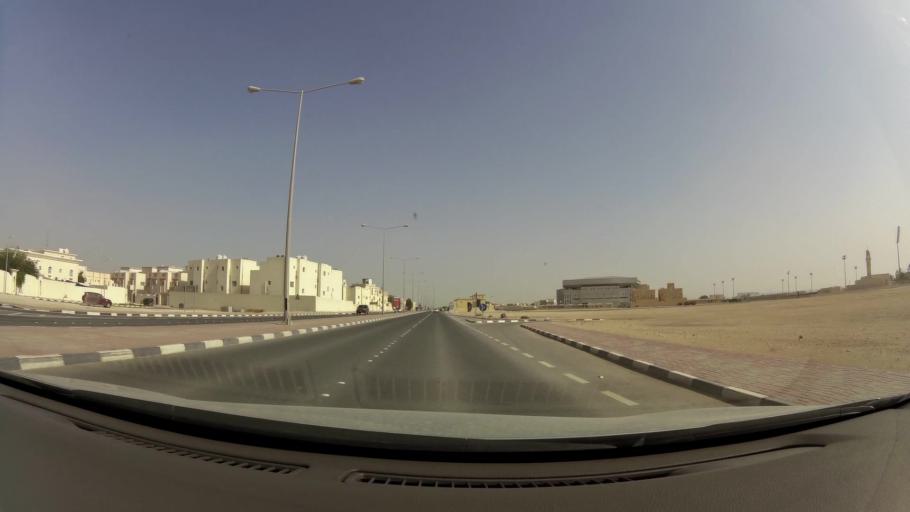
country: QA
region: Baladiyat ar Rayyan
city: Ar Rayyan
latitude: 25.3486
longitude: 51.4430
